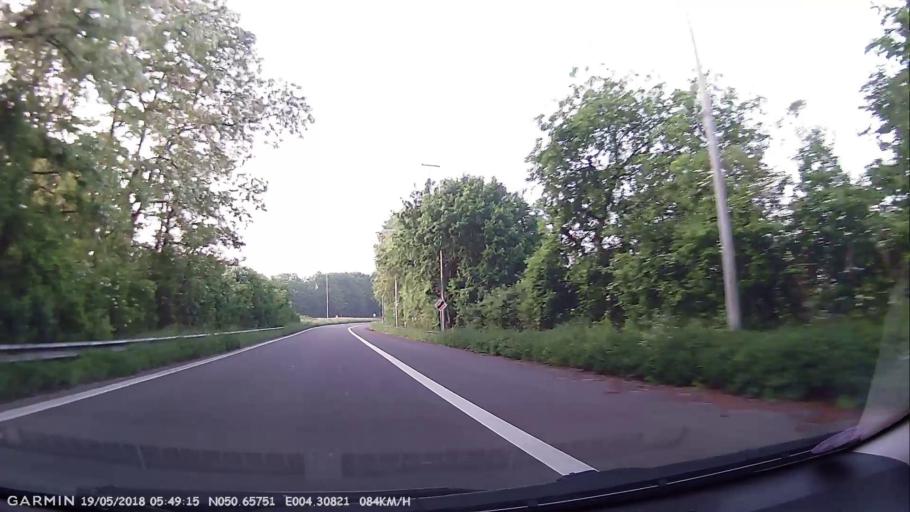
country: BE
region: Wallonia
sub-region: Province du Brabant Wallon
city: Braine-le-Chateau
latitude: 50.6573
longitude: 4.3084
